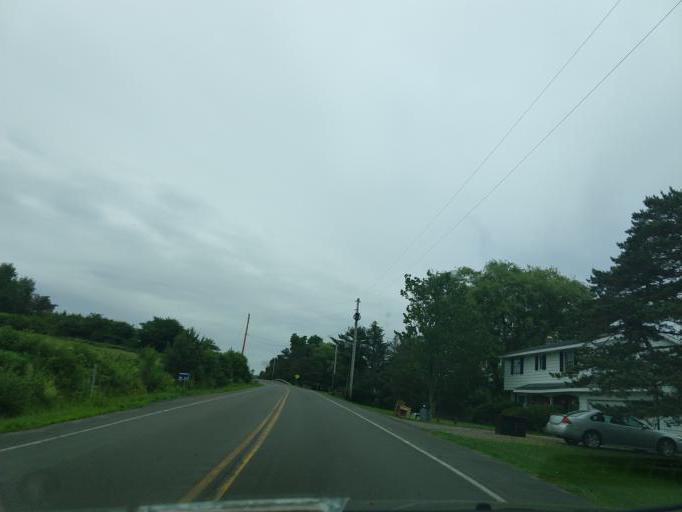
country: US
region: New York
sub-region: Tompkins County
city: Dryden
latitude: 42.4942
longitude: -76.2231
